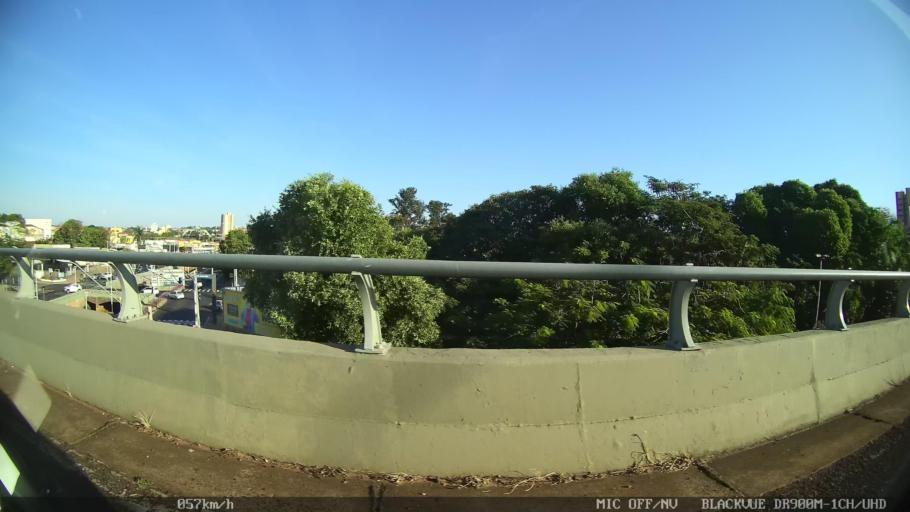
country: BR
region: Sao Paulo
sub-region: Sao Jose Do Rio Preto
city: Sao Jose do Rio Preto
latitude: -20.8040
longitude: -49.3782
